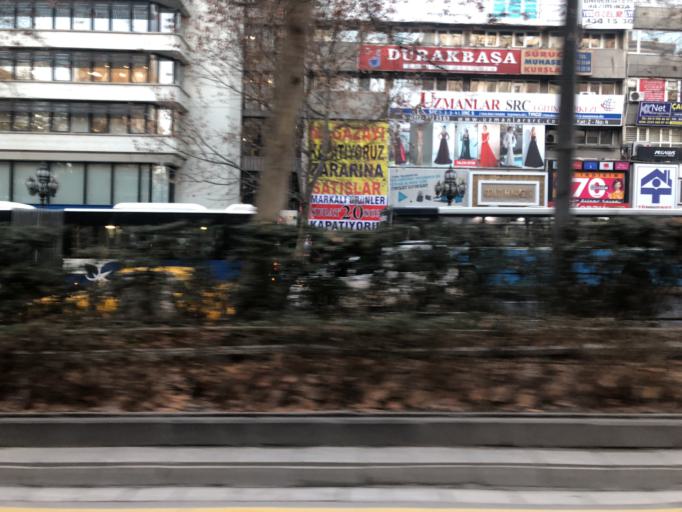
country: TR
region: Ankara
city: Ankara
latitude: 39.9228
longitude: 32.8541
